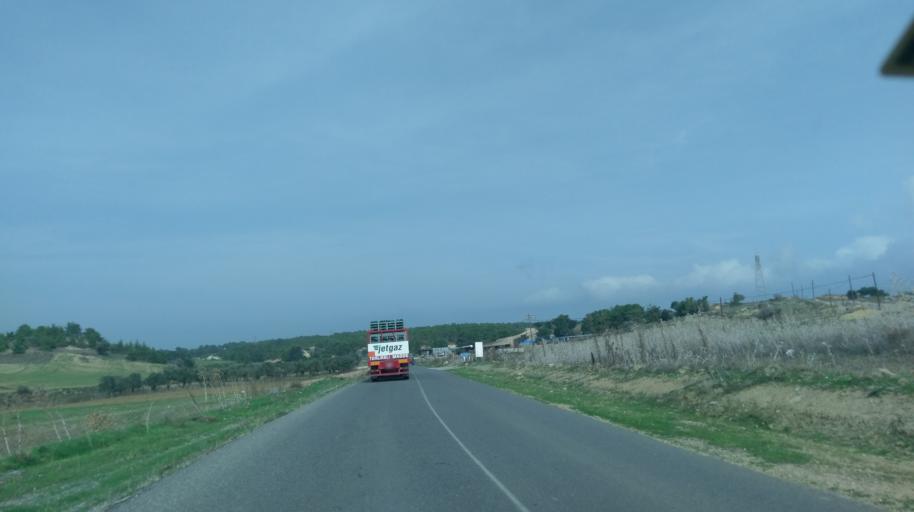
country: CY
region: Keryneia
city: Lapithos
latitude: 35.2938
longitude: 33.0885
